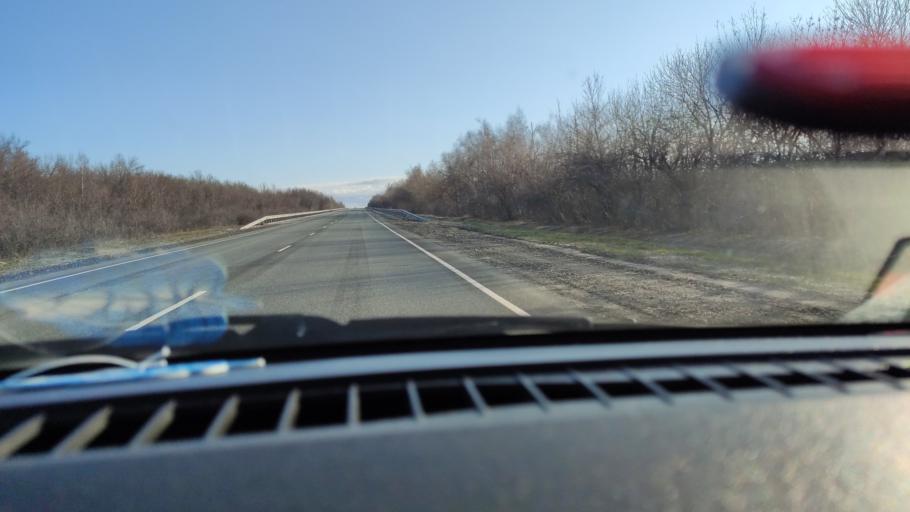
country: RU
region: Saratov
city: Khvalynsk
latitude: 52.6173
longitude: 48.1681
